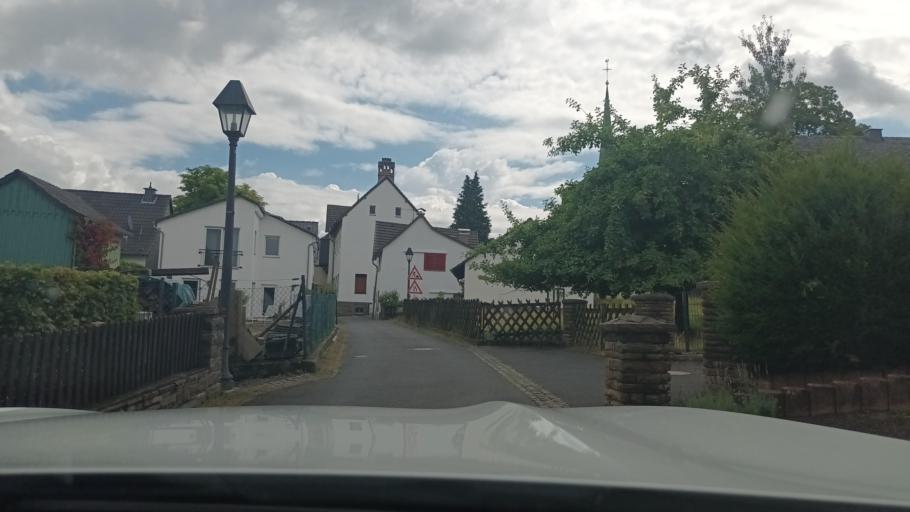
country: DE
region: North Rhine-Westphalia
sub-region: Regierungsbezirk Koln
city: Hennef
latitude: 50.7613
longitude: 7.3622
